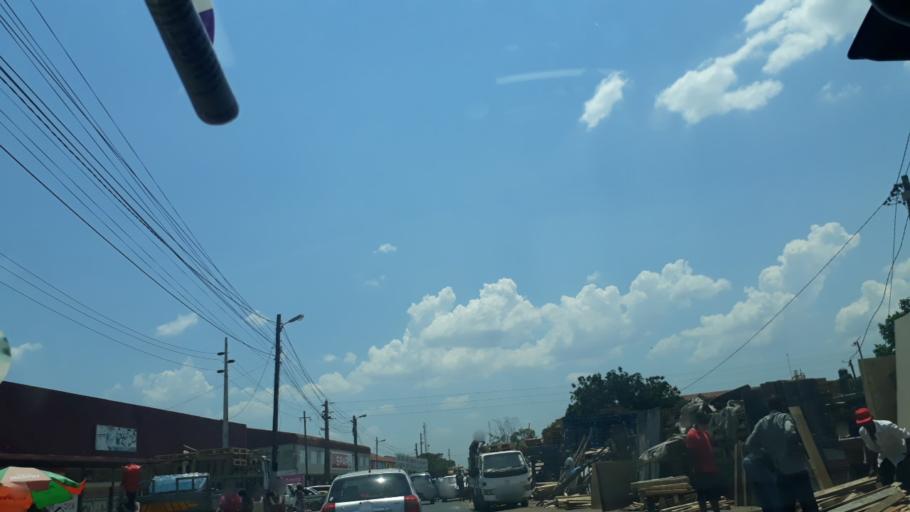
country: MZ
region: Maputo City
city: Maputo
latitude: -25.9354
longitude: 32.5557
